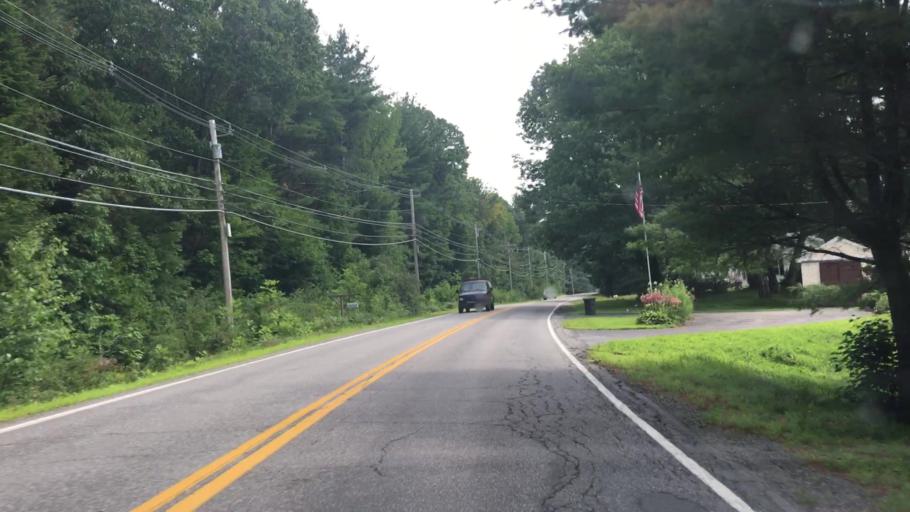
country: US
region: Maine
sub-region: Kennebec County
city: Winslow
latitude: 44.5206
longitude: -69.6308
